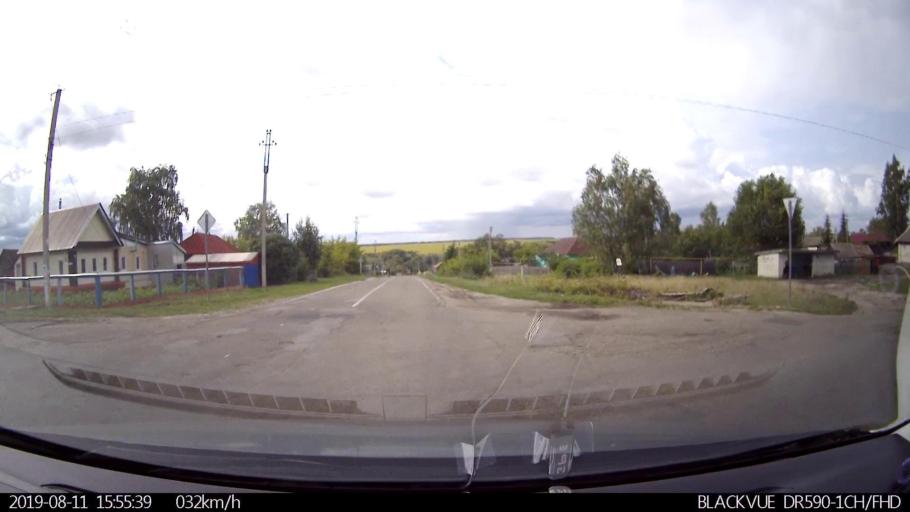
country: RU
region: Ulyanovsk
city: Ignatovka
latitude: 53.9460
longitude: 47.6530
